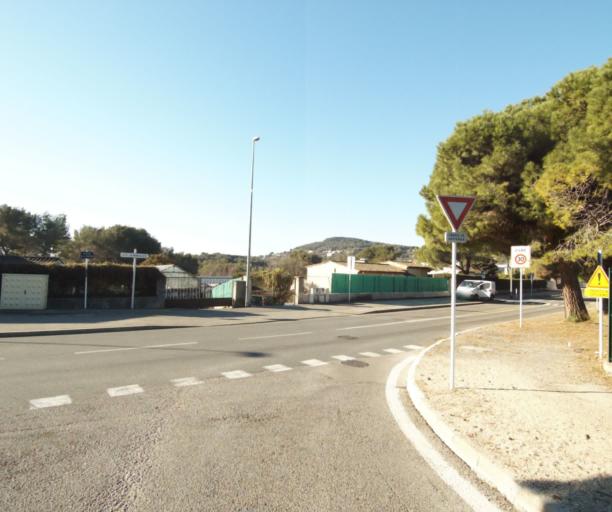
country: FR
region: Provence-Alpes-Cote d'Azur
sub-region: Departement des Alpes-Maritimes
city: Vallauris
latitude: 43.5970
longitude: 7.0762
